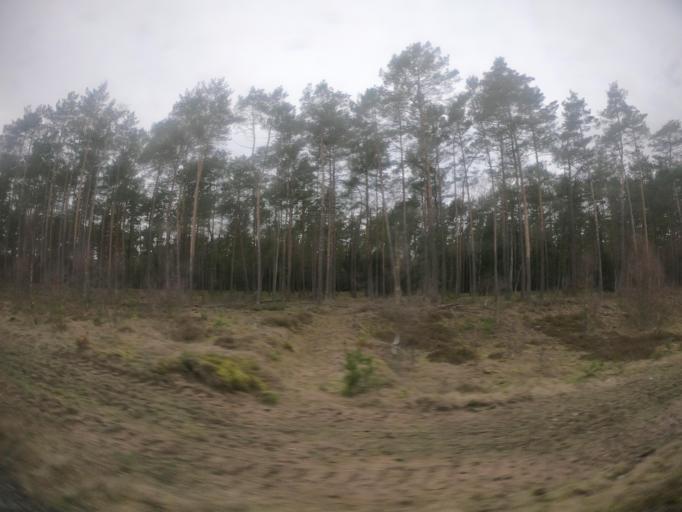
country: PL
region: Pomeranian Voivodeship
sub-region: Powiat czluchowski
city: Czarne
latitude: 53.7648
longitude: 16.8539
